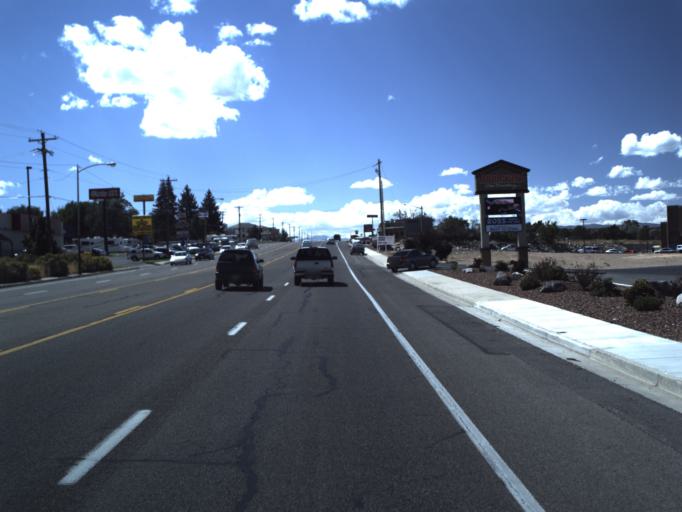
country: US
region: Utah
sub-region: Iron County
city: Cedar City
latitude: 37.6610
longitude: -113.0708
